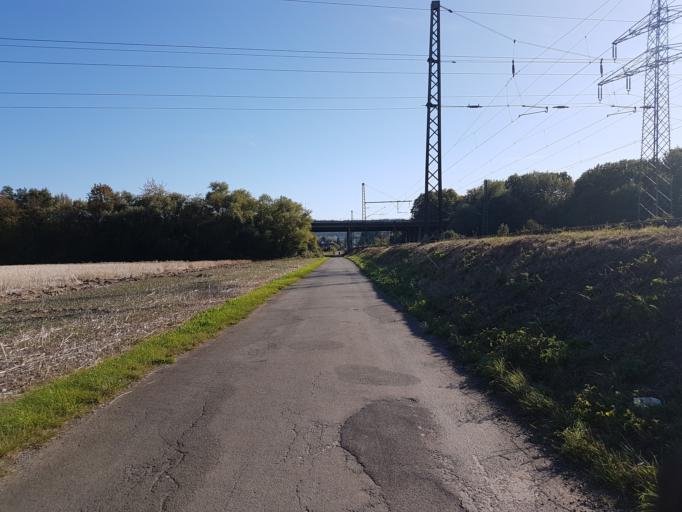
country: DE
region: North Rhine-Westphalia
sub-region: Regierungsbezirk Detmold
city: Minden
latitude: 52.2739
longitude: 8.9330
